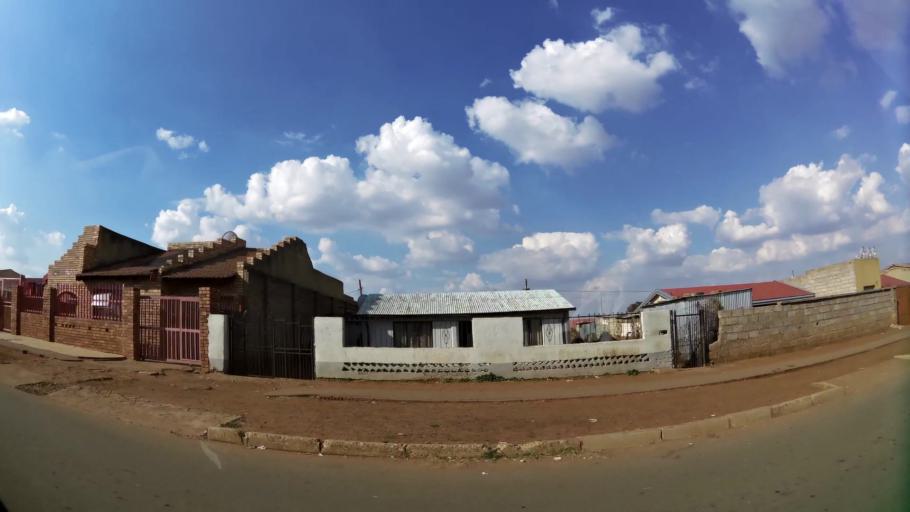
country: ZA
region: Gauteng
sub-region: City of Johannesburg Metropolitan Municipality
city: Soweto
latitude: -26.2195
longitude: 27.8678
